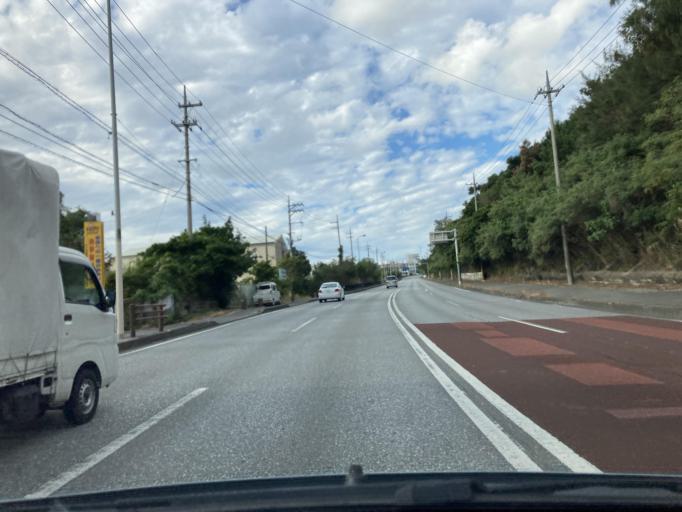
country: JP
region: Okinawa
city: Ishikawa
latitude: 26.4002
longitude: 127.8313
